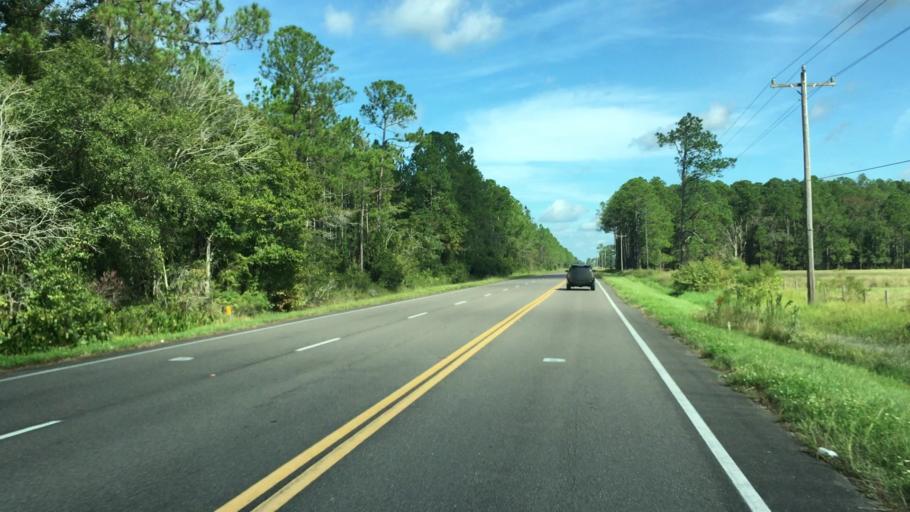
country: US
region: Florida
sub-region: Alachua County
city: Gainesville
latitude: 29.7447
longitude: -82.2771
